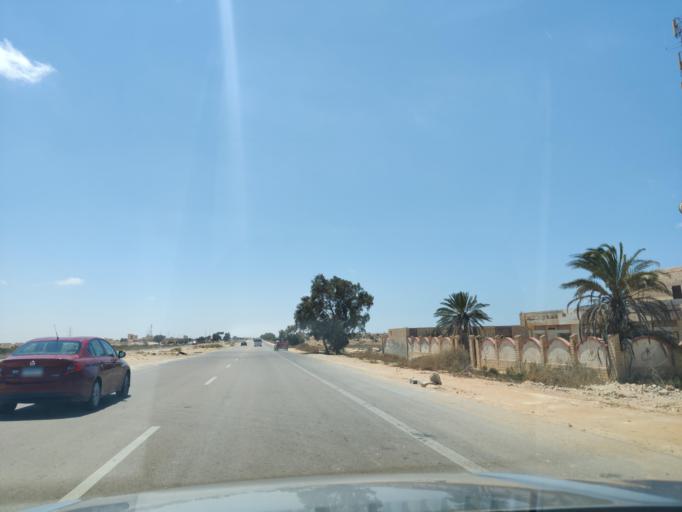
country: EG
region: Muhafazat Matruh
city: Al `Alamayn
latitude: 31.0696
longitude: 28.1360
